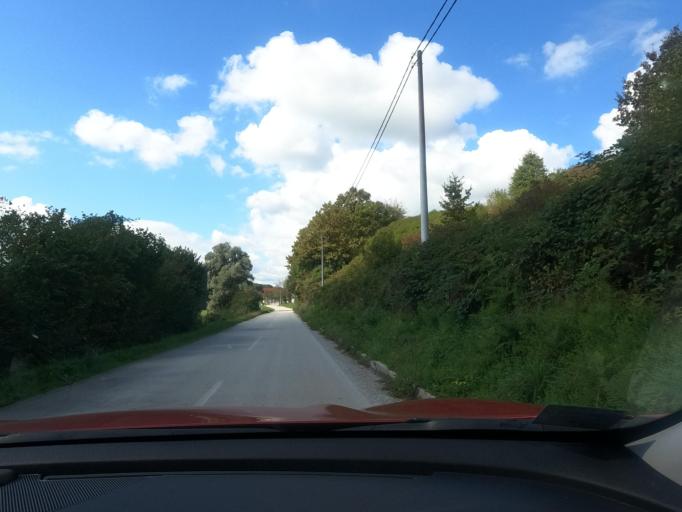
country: BA
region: Federation of Bosnia and Herzegovina
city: Velika Kladusa
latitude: 45.2112
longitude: 15.8134
